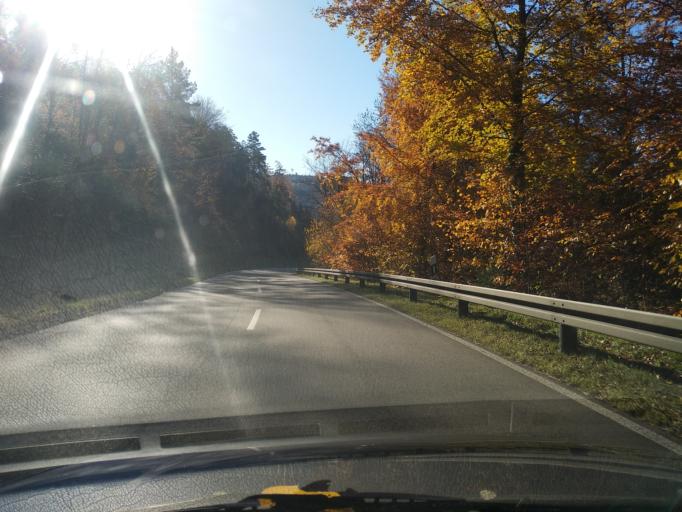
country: DE
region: Baden-Wuerttemberg
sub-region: Karlsruhe Region
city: Bad Liebenzell
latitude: 48.7776
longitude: 8.7364
